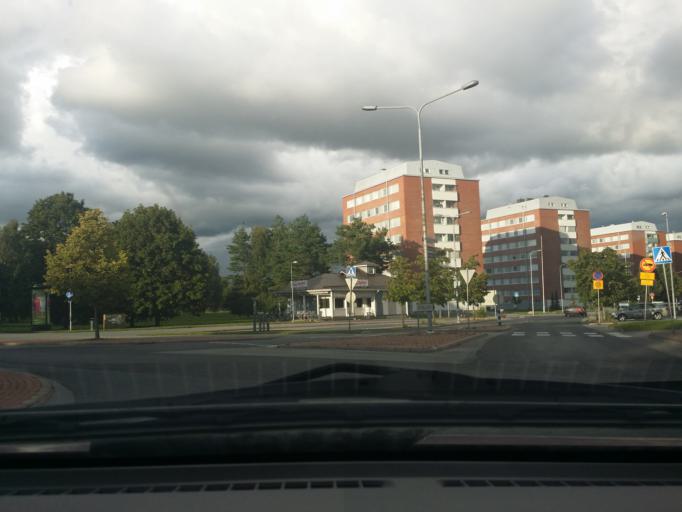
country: FI
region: Satakunta
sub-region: Pori
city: Pori
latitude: 61.4880
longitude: 21.8033
